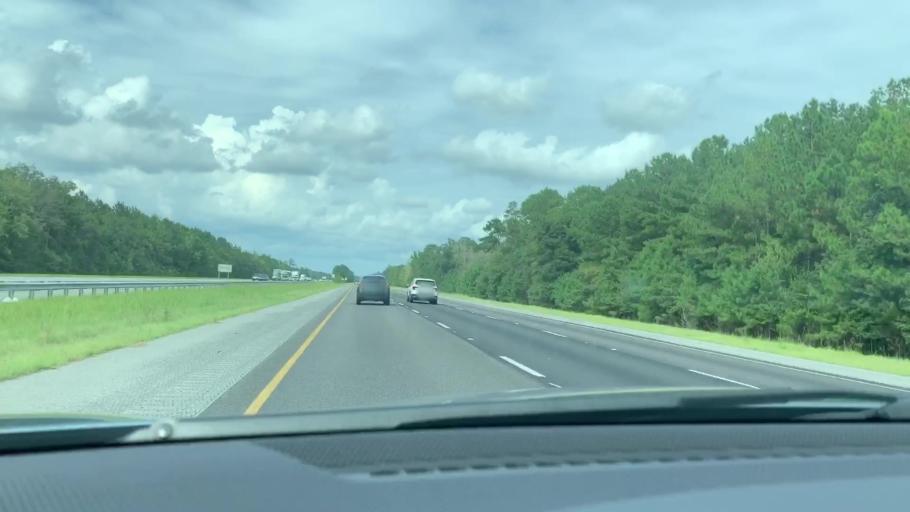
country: US
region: Georgia
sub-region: Liberty County
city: Midway
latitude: 31.6747
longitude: -81.3920
